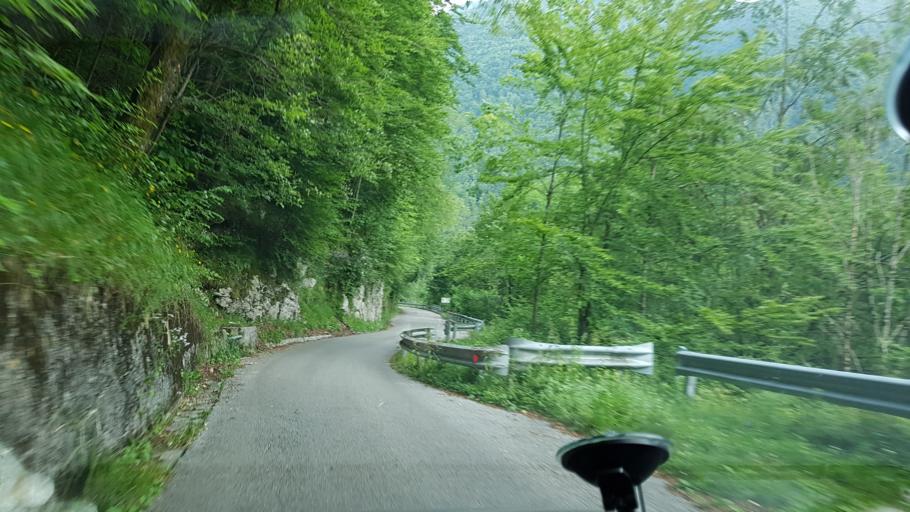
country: IT
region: Friuli Venezia Giulia
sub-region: Provincia di Udine
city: Taipana
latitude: 46.3098
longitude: 13.3954
